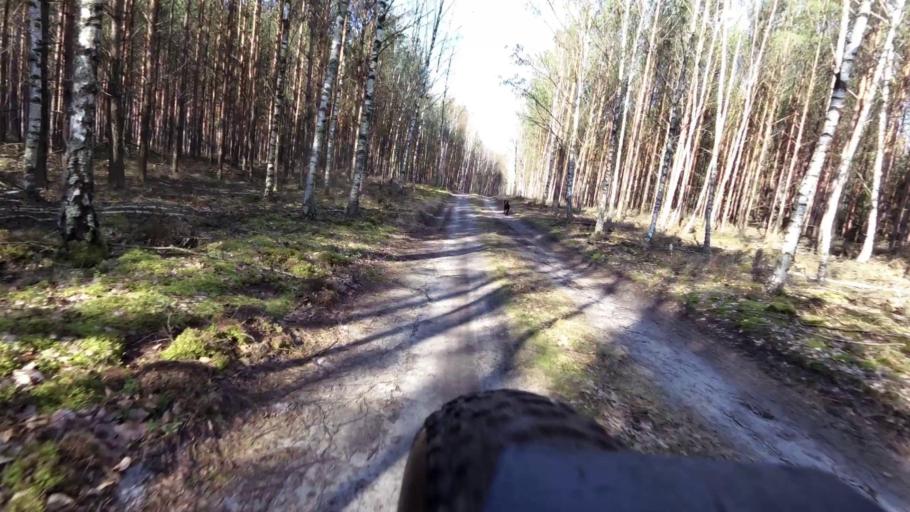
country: PL
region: Lubusz
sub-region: Powiat sulecinski
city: Torzym
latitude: 52.2189
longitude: 14.9930
